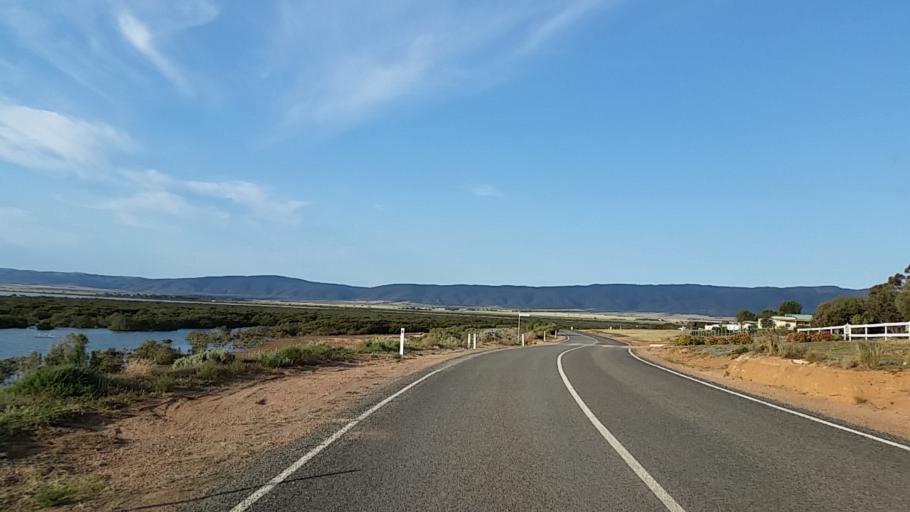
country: AU
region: South Australia
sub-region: Port Pirie City and Dists
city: Port Pirie
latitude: -33.1007
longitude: 138.0278
